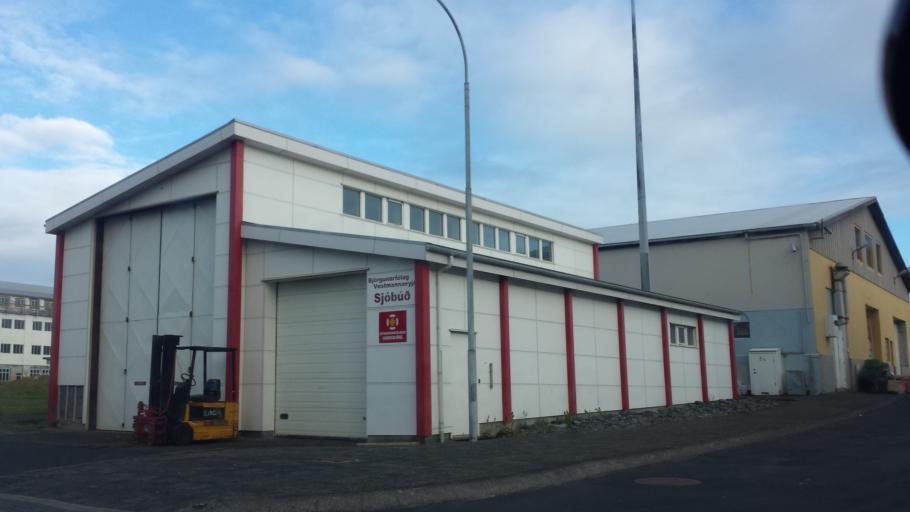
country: IS
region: South
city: Vestmannaeyjar
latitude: 63.4435
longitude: -20.2719
